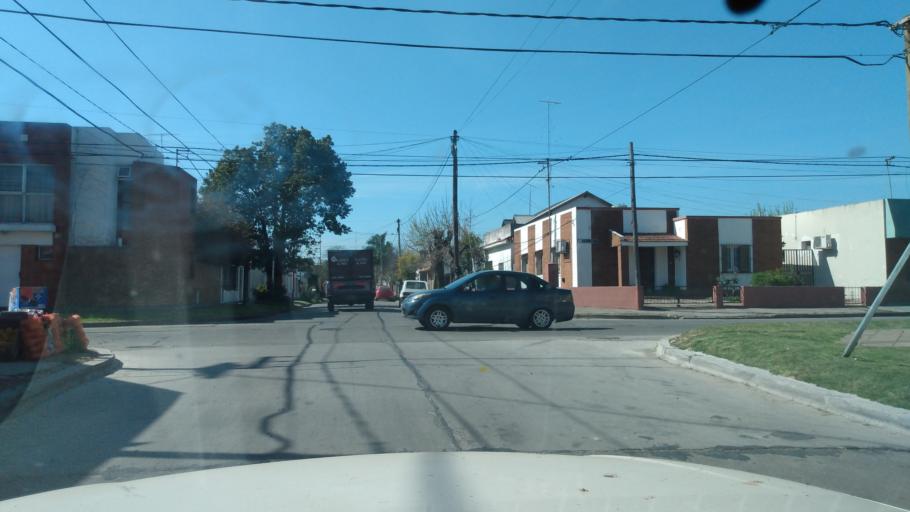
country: AR
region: Buenos Aires
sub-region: Partido de Lujan
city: Lujan
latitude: -34.5729
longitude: -59.1011
